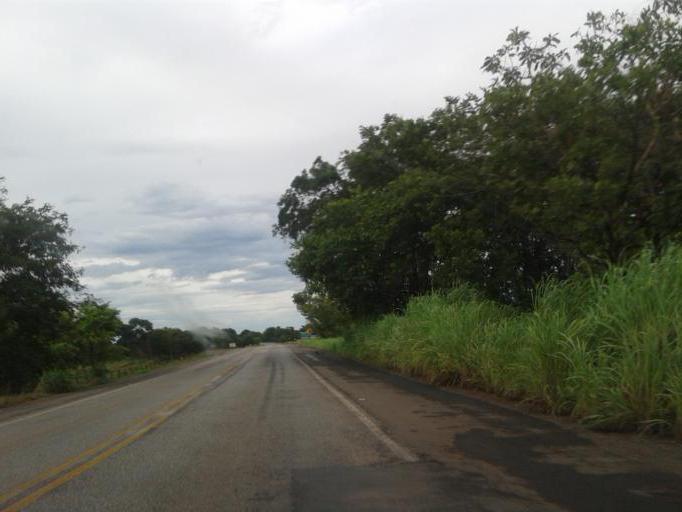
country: BR
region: Goias
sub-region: Mozarlandia
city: Mozarlandia
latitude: -14.8078
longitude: -50.5329
